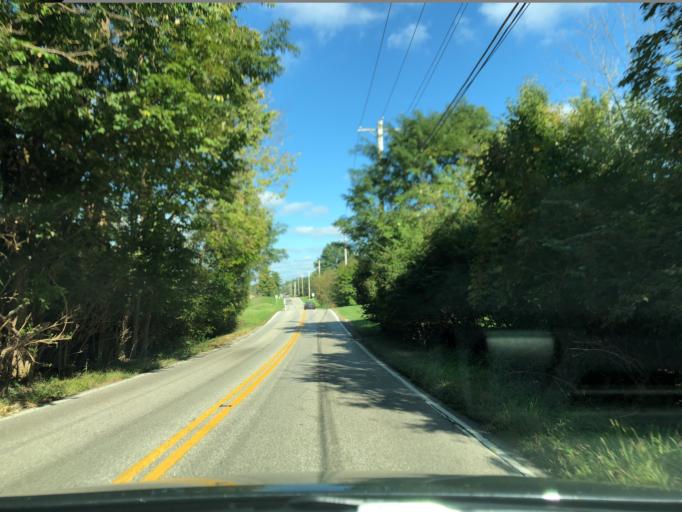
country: US
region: Ohio
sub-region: Hamilton County
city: Loveland
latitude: 39.2326
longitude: -84.2512
